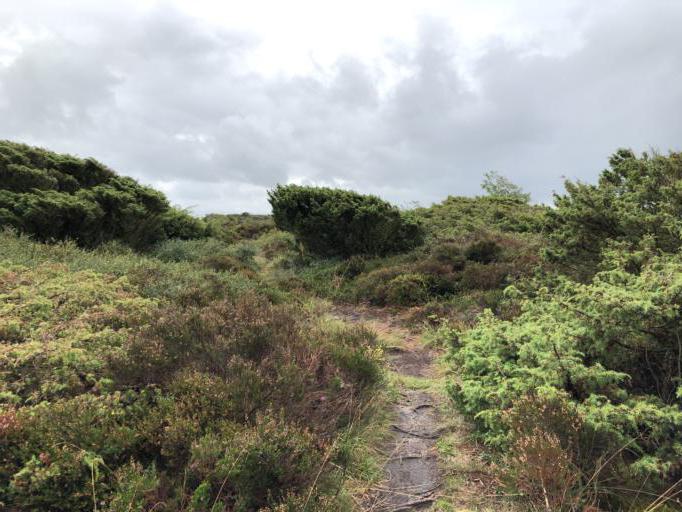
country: DK
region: Central Jutland
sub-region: Holstebro Kommune
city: Ulfborg
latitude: 56.2569
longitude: 8.4200
